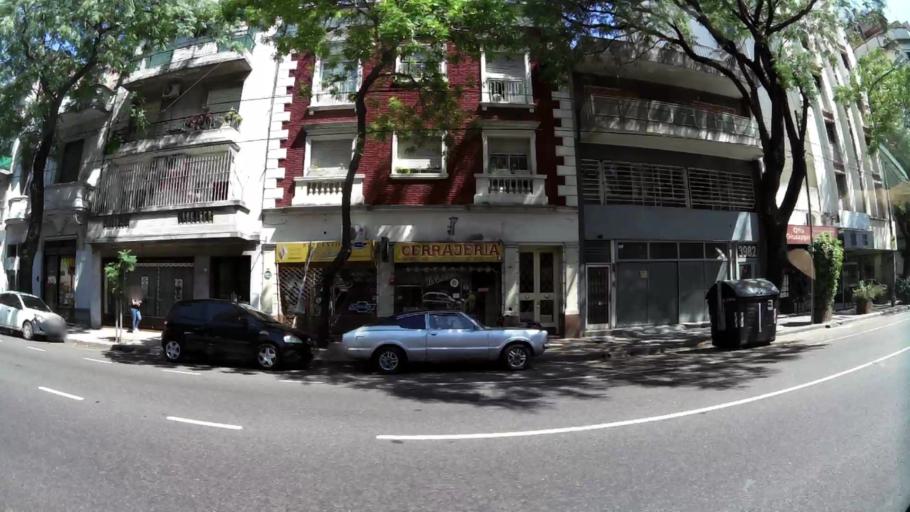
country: AR
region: Buenos Aires F.D.
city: Buenos Aires
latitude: -34.6214
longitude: -58.4219
